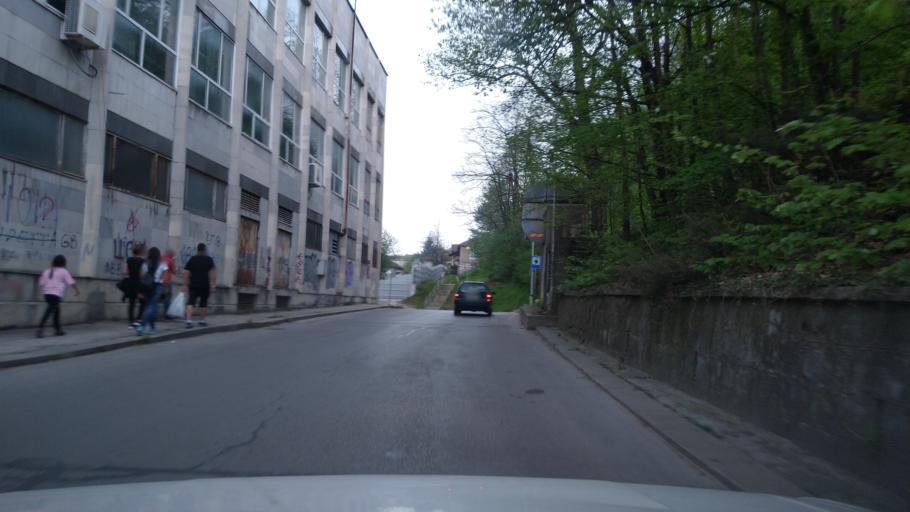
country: BG
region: Gabrovo
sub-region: Obshtina Gabrovo
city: Gabrovo
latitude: 42.8662
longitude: 25.3167
